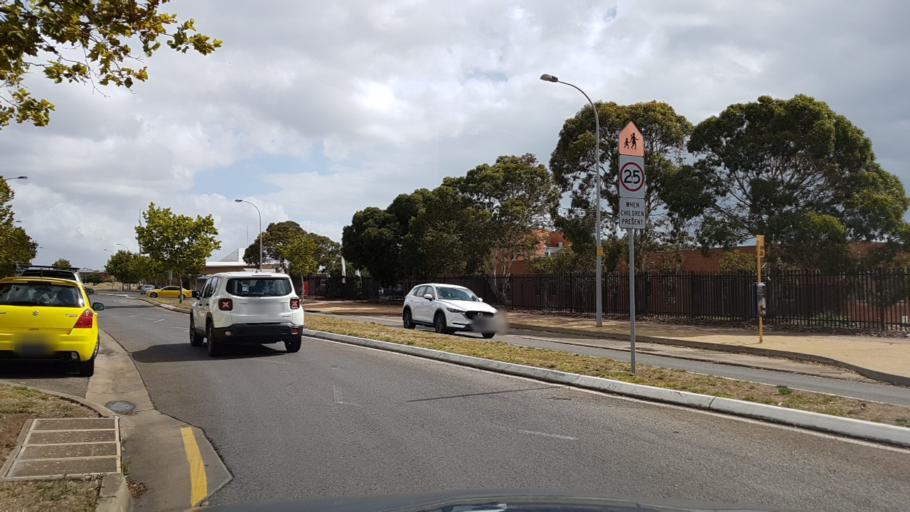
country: AU
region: South Australia
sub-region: Onkaparinga
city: Seaford
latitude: -35.1851
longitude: 138.4810
